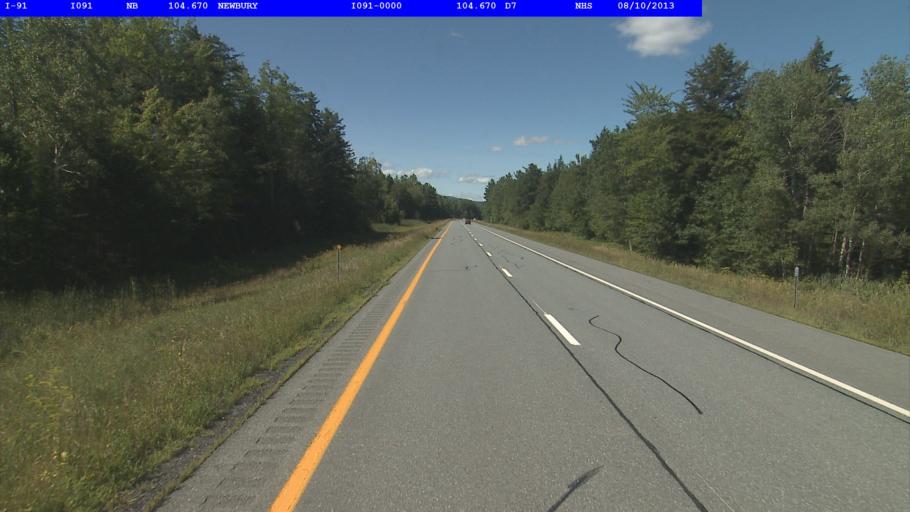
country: US
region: New Hampshire
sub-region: Grafton County
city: Haverhill
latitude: 44.0806
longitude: -72.1119
